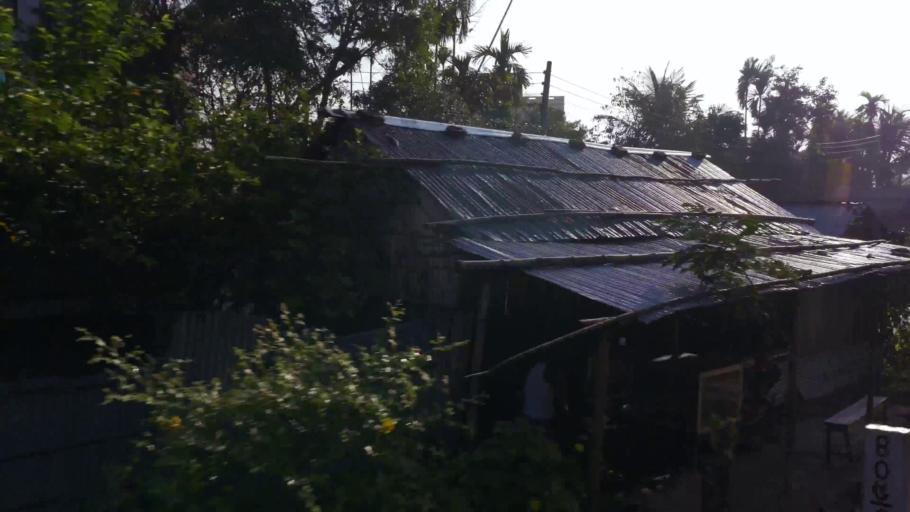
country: BD
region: Dhaka
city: Jamalpur
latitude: 24.9010
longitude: 89.9775
